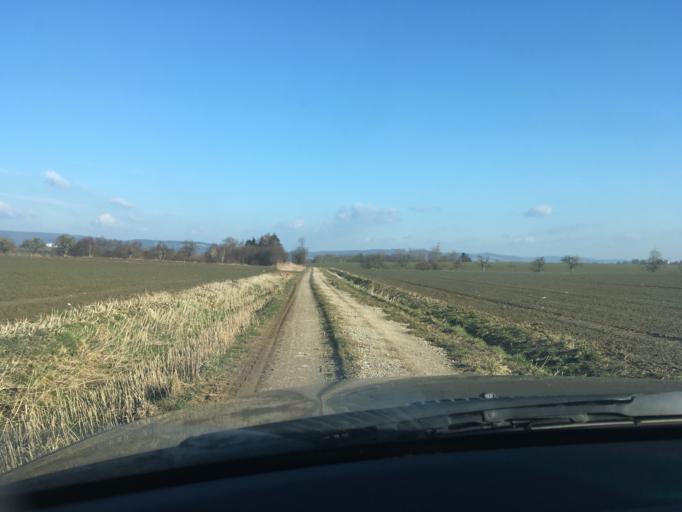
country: DE
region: Lower Saxony
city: Einbeck
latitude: 51.8034
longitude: 9.8196
